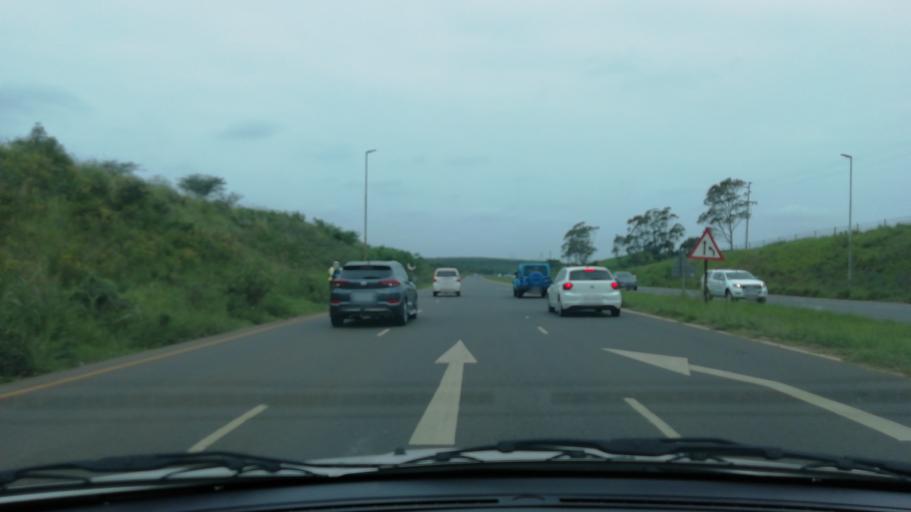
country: ZA
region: KwaZulu-Natal
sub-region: uThungulu District Municipality
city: Empangeni
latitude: -28.7668
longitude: 31.9163
